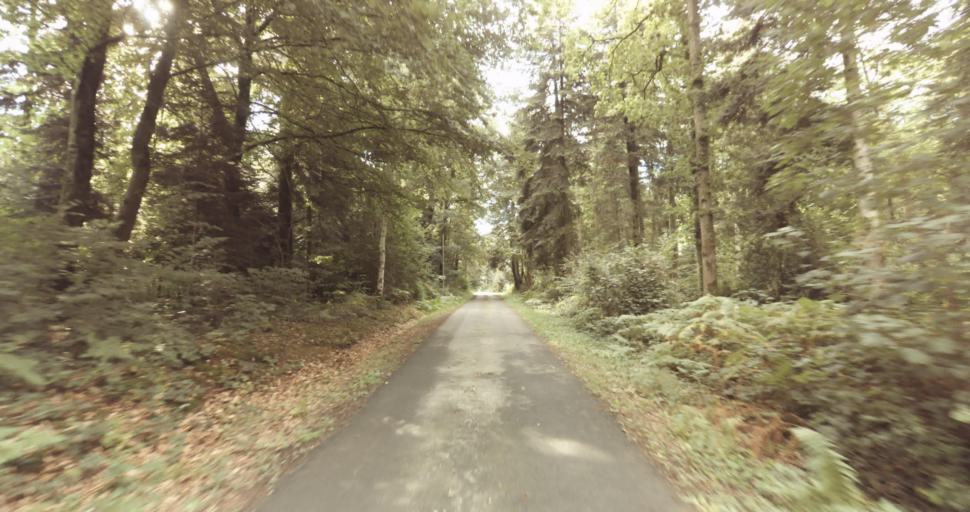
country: FR
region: Lower Normandy
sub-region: Departement de l'Orne
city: Gace
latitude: 48.8256
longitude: 0.2319
